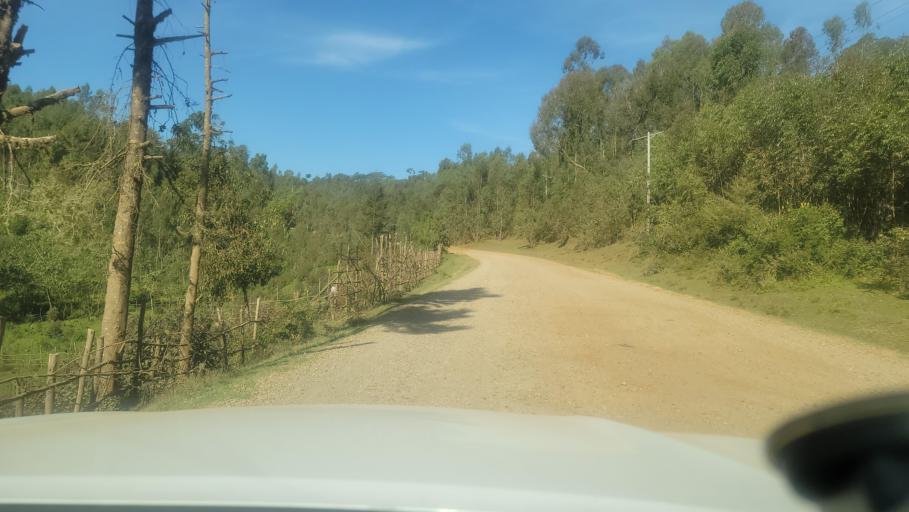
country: ET
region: Oromiya
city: Agaro
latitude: 7.8002
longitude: 36.4705
